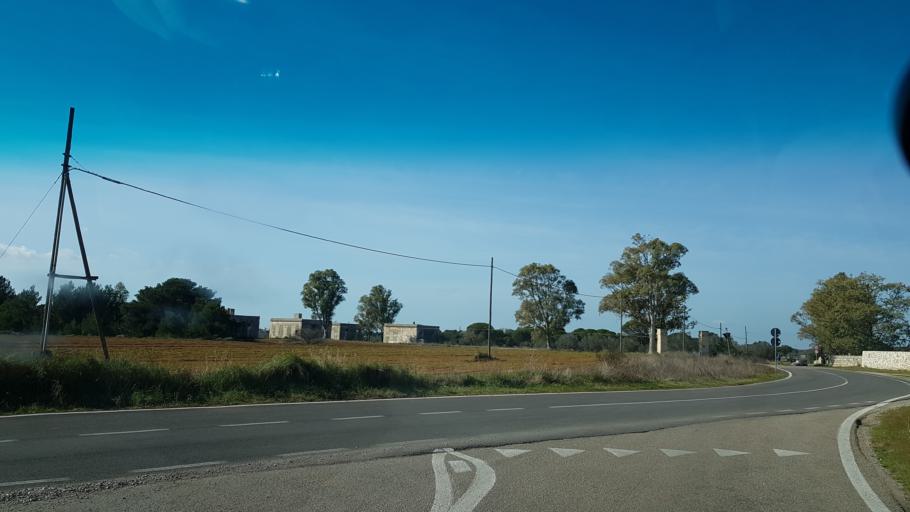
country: IT
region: Apulia
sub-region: Provincia di Lecce
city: Arnesano
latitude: 40.3507
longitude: 18.1093
